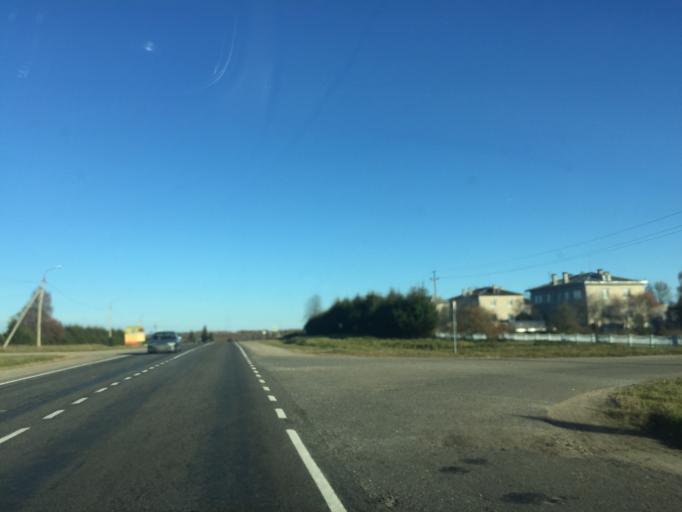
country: BY
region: Vitebsk
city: Dzisna
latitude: 55.3511
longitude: 28.3207
